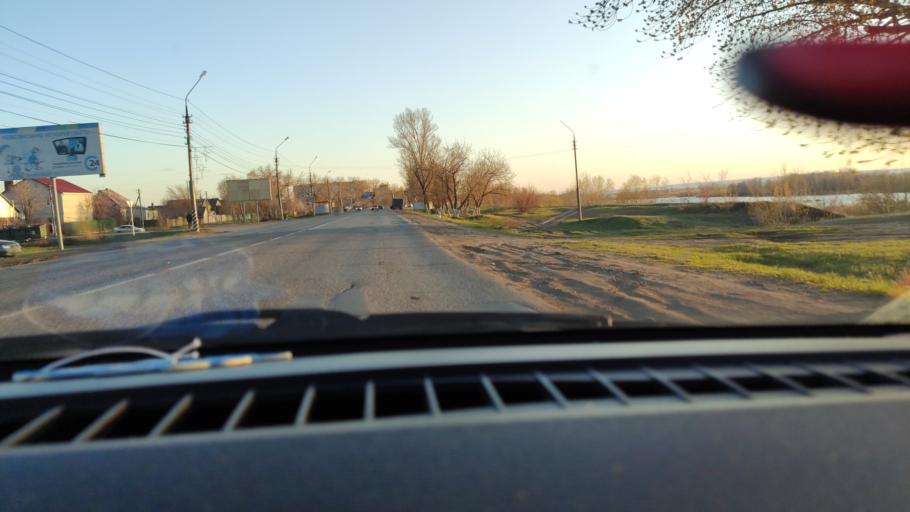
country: RU
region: Saratov
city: Engel's
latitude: 51.4492
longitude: 46.0801
